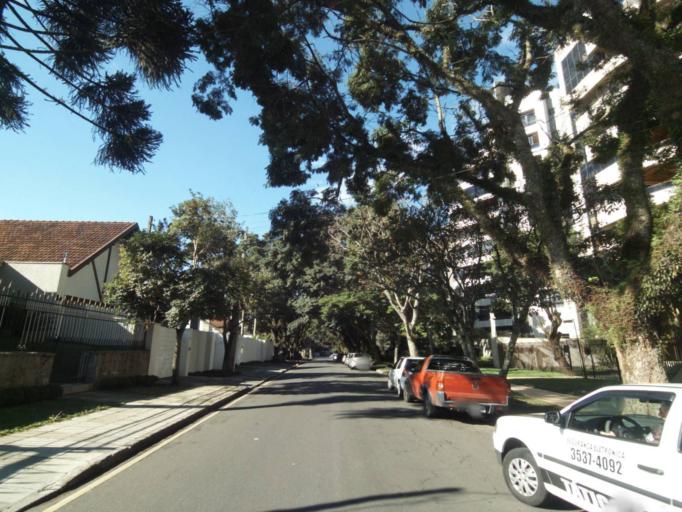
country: BR
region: Parana
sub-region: Curitiba
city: Curitiba
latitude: -25.4090
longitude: -49.2472
